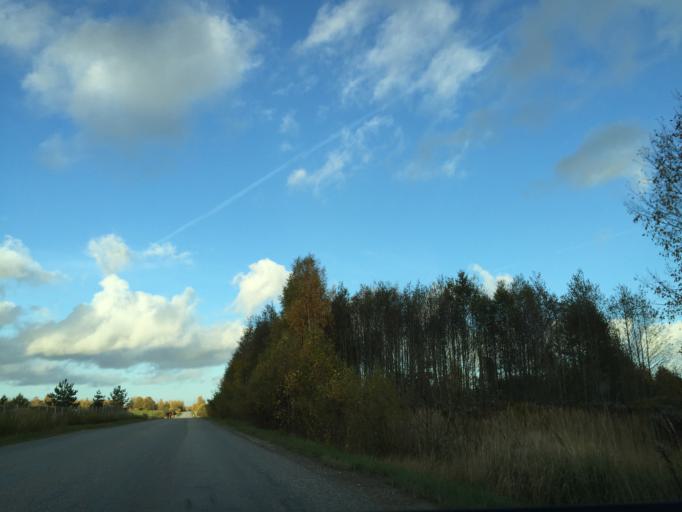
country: LV
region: Ogre
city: Jumprava
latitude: 56.7856
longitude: 25.0239
